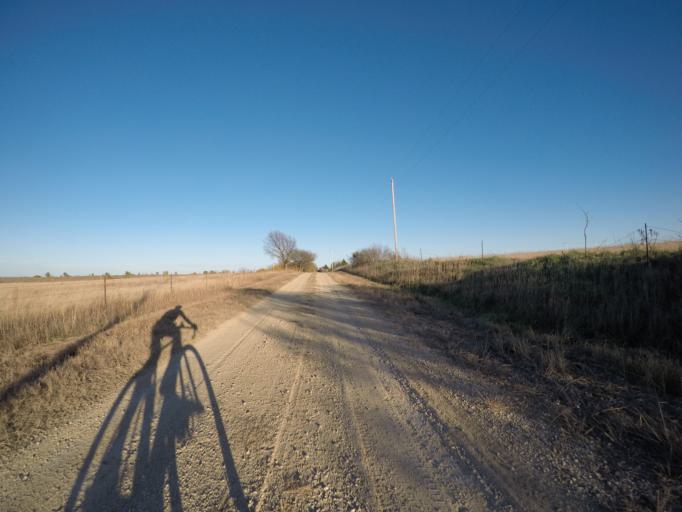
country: US
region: Kansas
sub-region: Riley County
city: Manhattan
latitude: 39.2544
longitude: -96.6646
